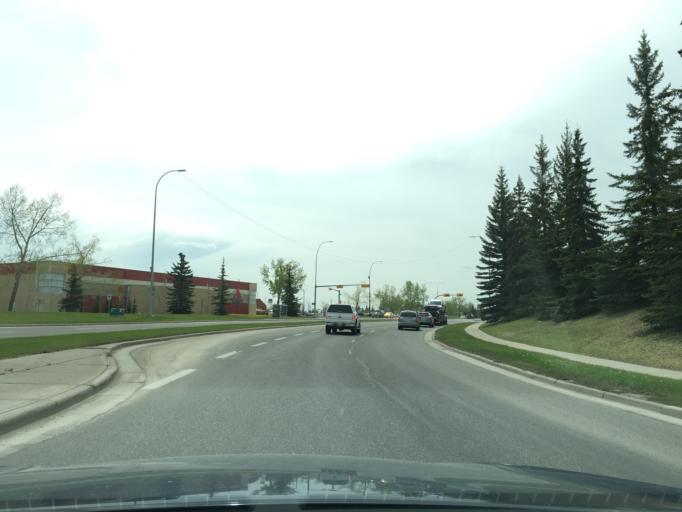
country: CA
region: Alberta
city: Calgary
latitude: 50.9535
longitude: -114.0609
